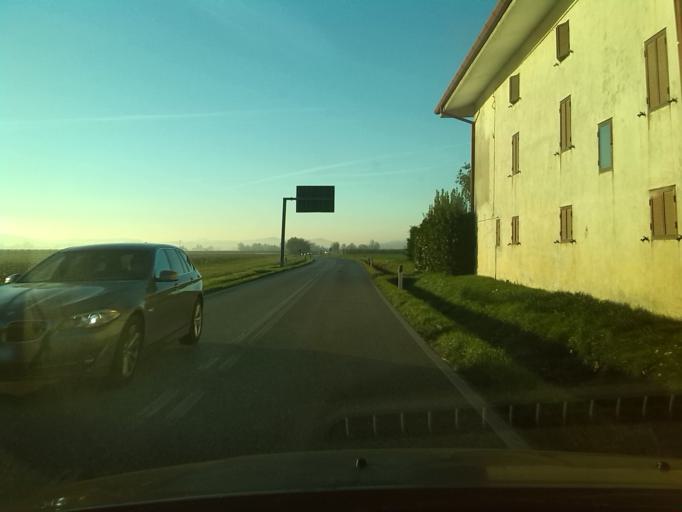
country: IT
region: Friuli Venezia Giulia
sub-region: Provincia di Udine
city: Cividale del Friuli
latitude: 46.0631
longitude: 13.4345
